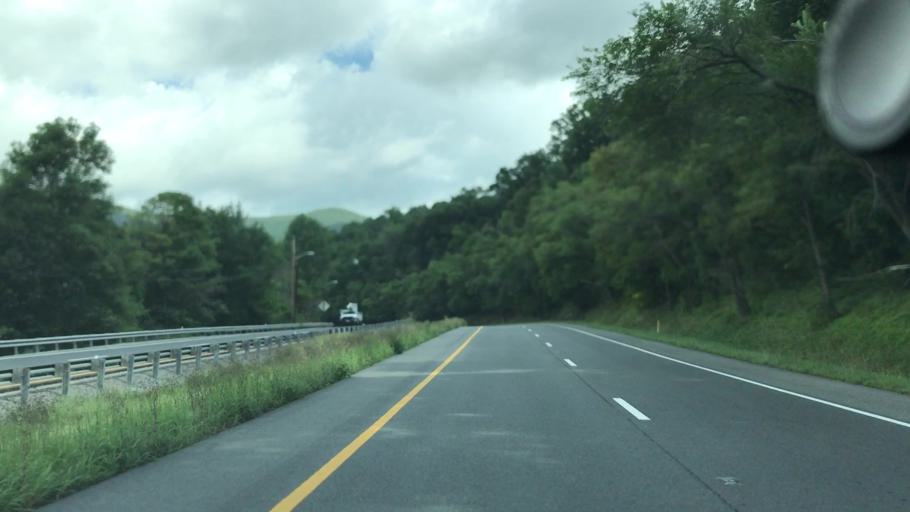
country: US
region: Virginia
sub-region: Giles County
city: Pearisburg
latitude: 37.3445
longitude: -80.7592
